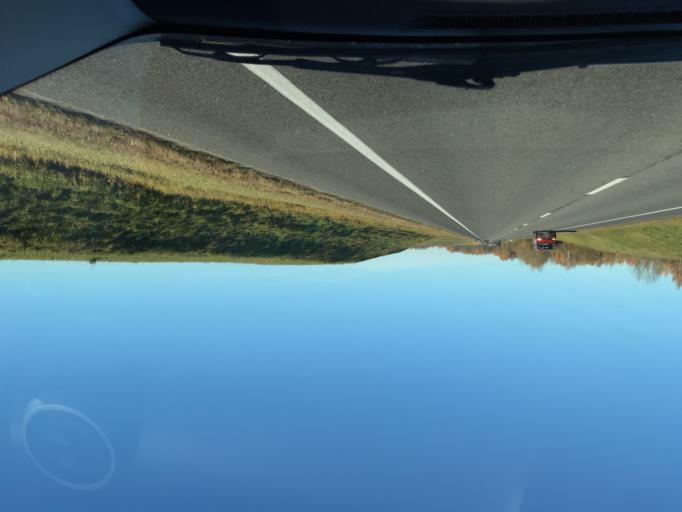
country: BY
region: Vitebsk
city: Vitebsk
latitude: 55.0664
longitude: 30.3097
